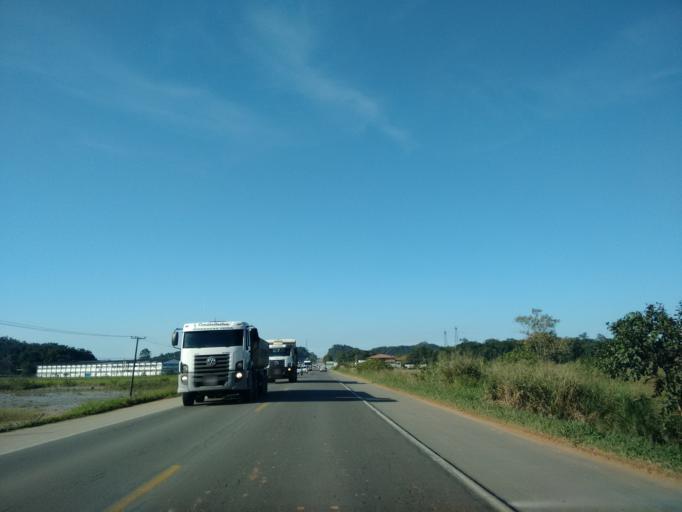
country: BR
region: Santa Catarina
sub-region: Guaramirim
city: Guaramirim
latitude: -26.4649
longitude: -48.9541
